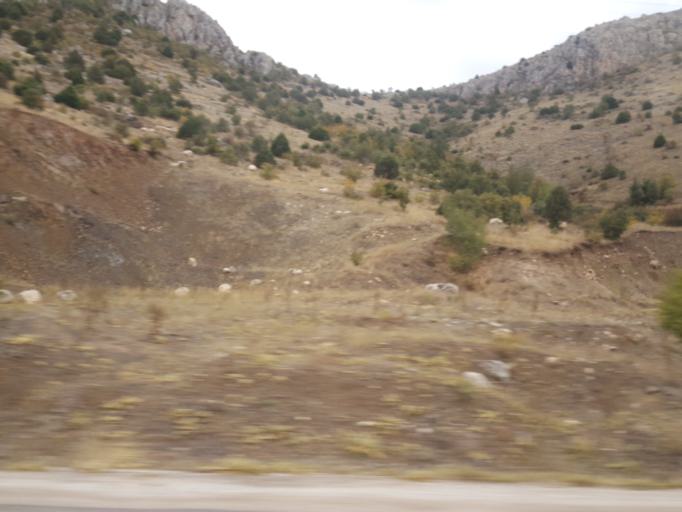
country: TR
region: Yozgat
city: Cekerek
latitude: 40.2112
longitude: 35.4960
